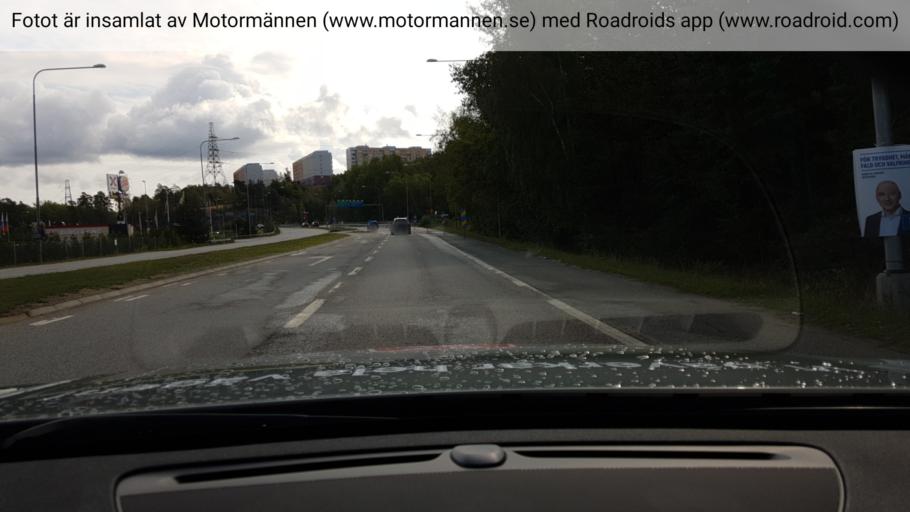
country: SE
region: Stockholm
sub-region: Botkyrka Kommun
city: Eriksberg
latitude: 59.2434
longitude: 17.8320
